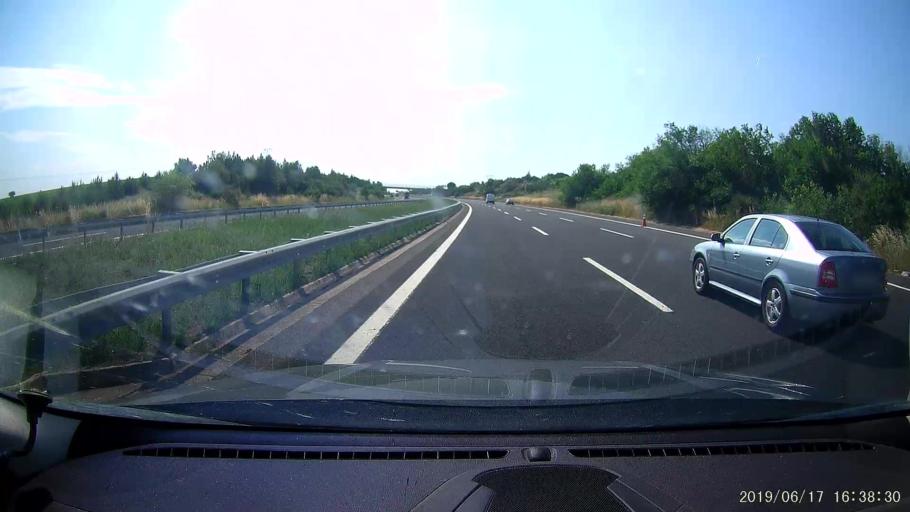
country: TR
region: Kirklareli
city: Luleburgaz
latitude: 41.4464
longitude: 27.4408
